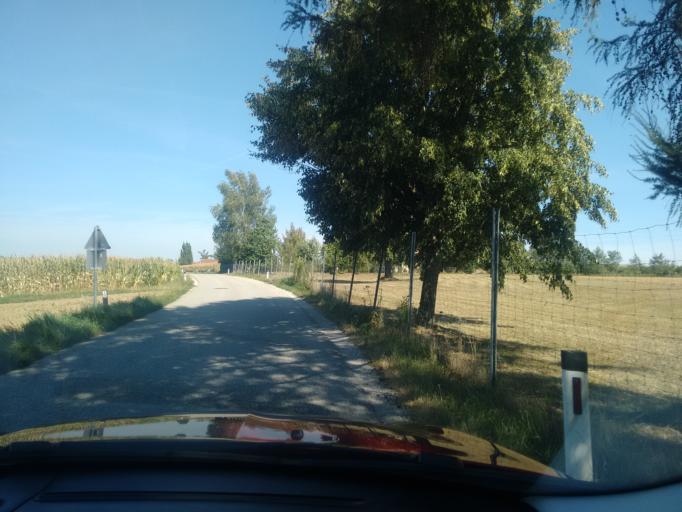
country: AT
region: Upper Austria
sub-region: Wels-Land
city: Steinhaus
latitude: 48.1074
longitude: 14.0269
